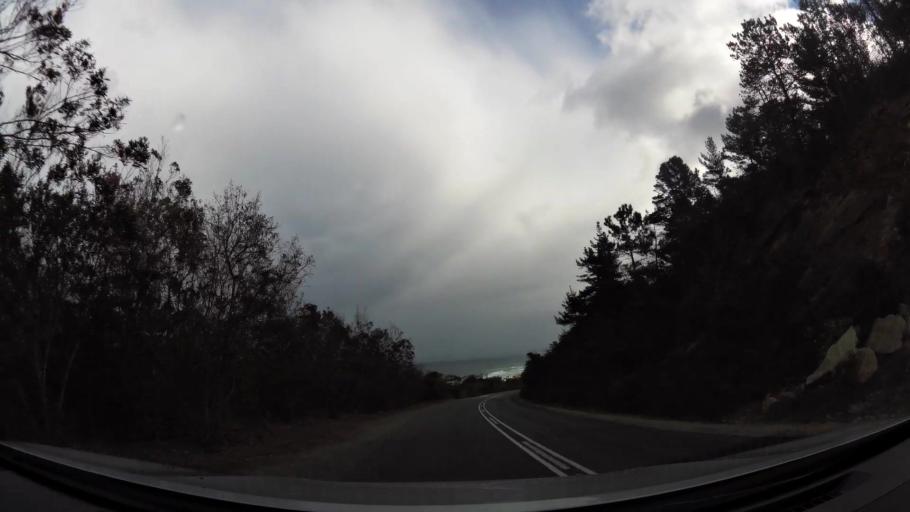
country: ZA
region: Western Cape
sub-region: Eden District Municipality
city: George
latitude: -34.0455
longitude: 22.3180
